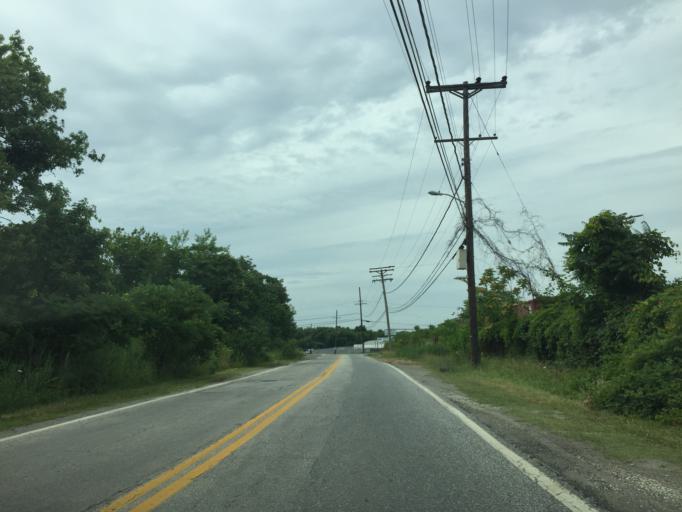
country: US
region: Maryland
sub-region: Baltimore County
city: Edgemere
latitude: 39.2735
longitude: -76.4615
